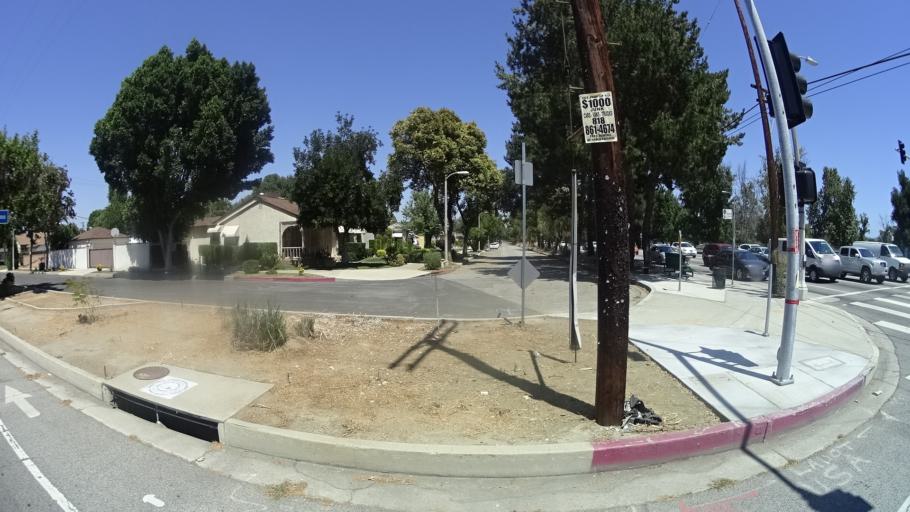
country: US
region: California
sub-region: Los Angeles County
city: Northridge
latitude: 34.1871
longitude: -118.5182
